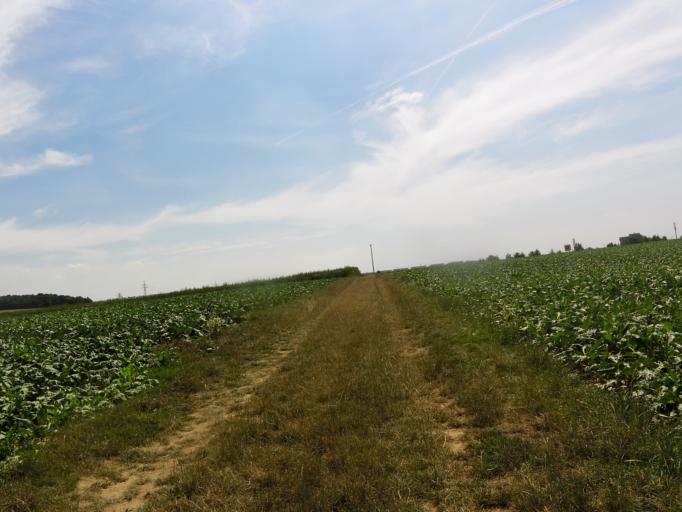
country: DE
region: Bavaria
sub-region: Regierungsbezirk Unterfranken
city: Estenfeld
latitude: 49.8057
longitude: 10.0054
